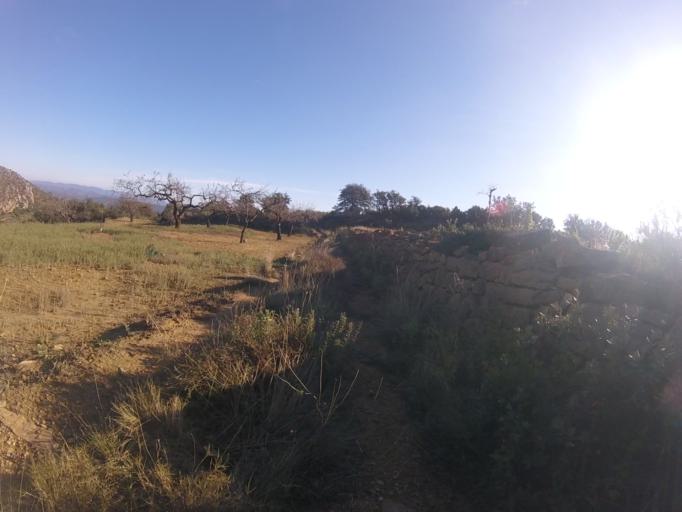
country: ES
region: Valencia
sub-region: Provincia de Castello
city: Sarratella
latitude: 40.2953
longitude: 0.0497
